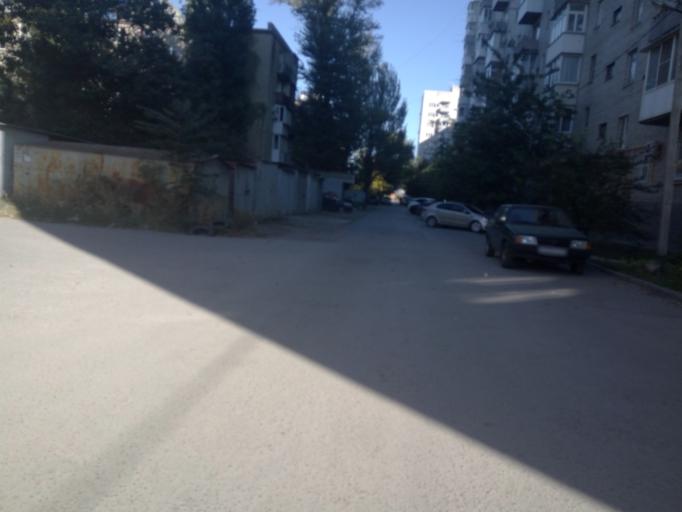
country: RU
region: Rostov
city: Bataysk
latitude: 47.1226
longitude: 39.7331
